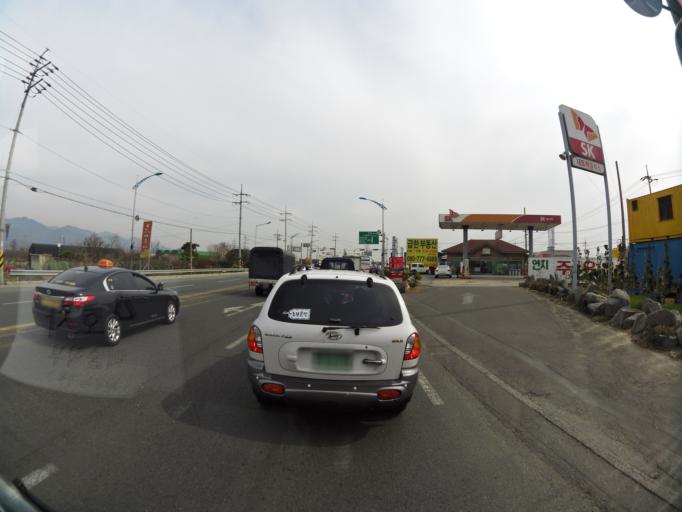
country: KR
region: Gyeongsangbuk-do
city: Hayang
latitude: 35.8716
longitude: 128.7794
